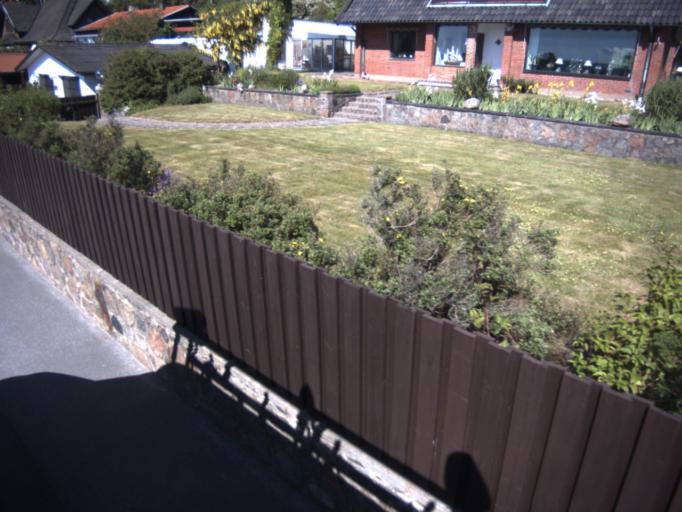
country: SE
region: Skane
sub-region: Helsingborg
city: Rydeback
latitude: 55.9613
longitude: 12.7580
